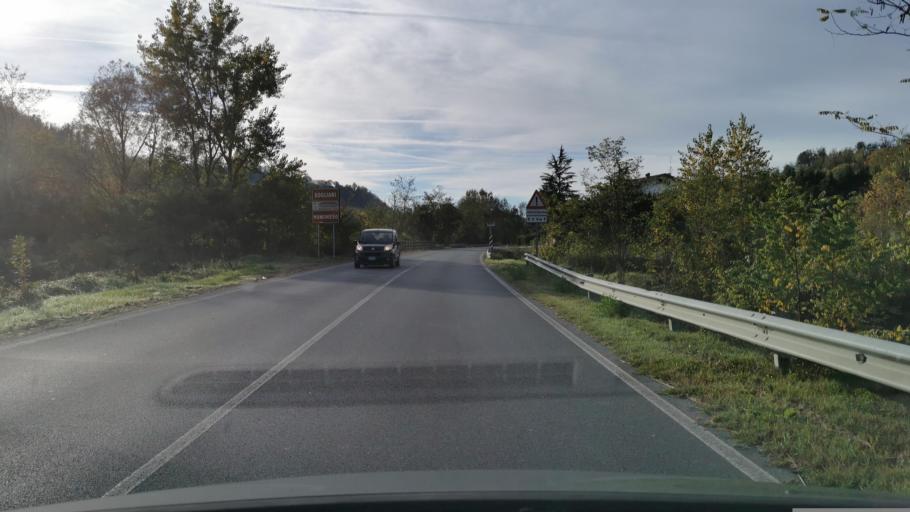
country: IT
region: Piedmont
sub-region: Provincia di Cuneo
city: Monchiero Borgonuovo
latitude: 44.5614
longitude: 7.9227
